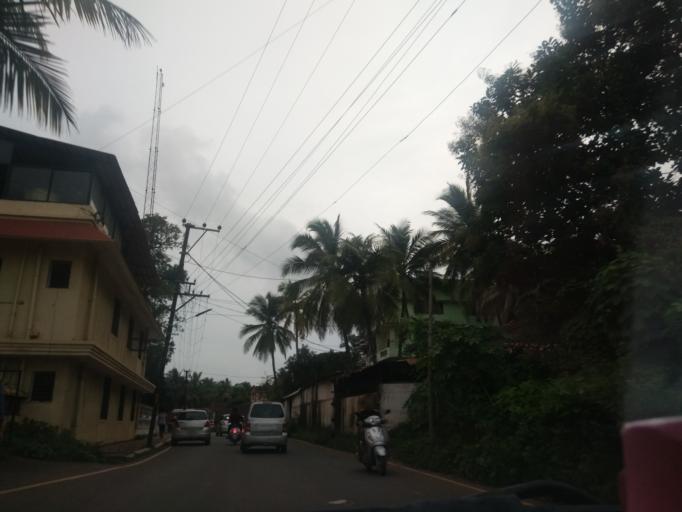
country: IN
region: Goa
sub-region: South Goa
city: Madgaon
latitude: 15.2577
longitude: 73.9669
